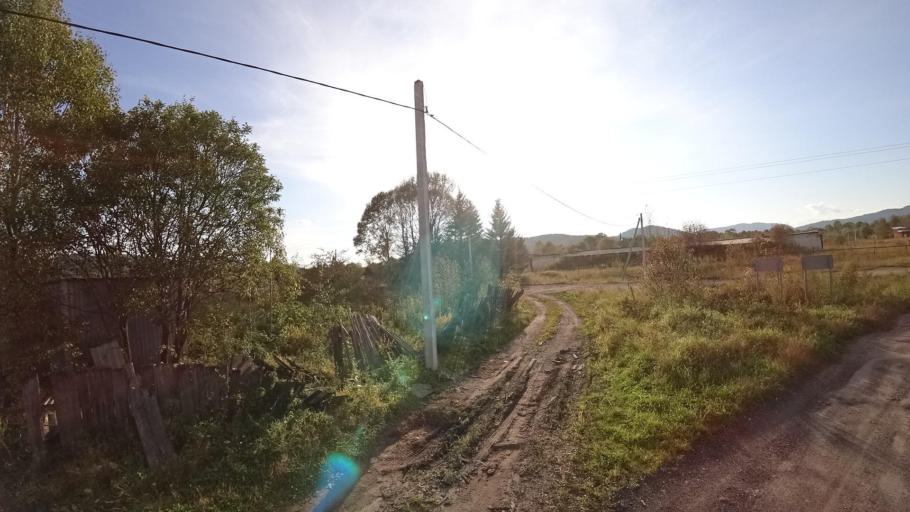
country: RU
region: Jewish Autonomous Oblast
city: Kul'dur
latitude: 49.1984
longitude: 131.6259
